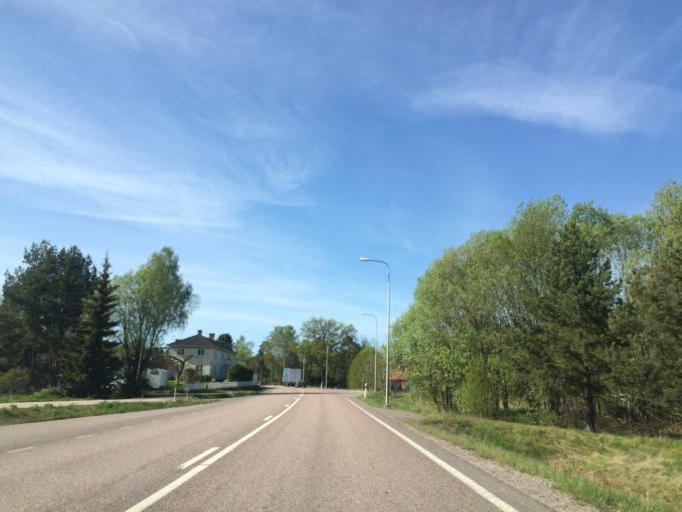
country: SE
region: Vaestmanland
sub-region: Kungsors Kommun
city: Kungsoer
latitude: 59.2826
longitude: 16.1179
